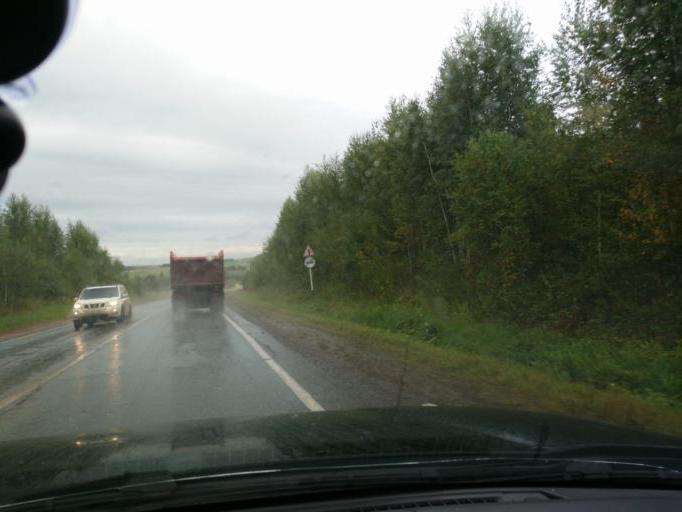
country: RU
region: Perm
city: Kultayevo
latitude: 57.8468
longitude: 55.8348
